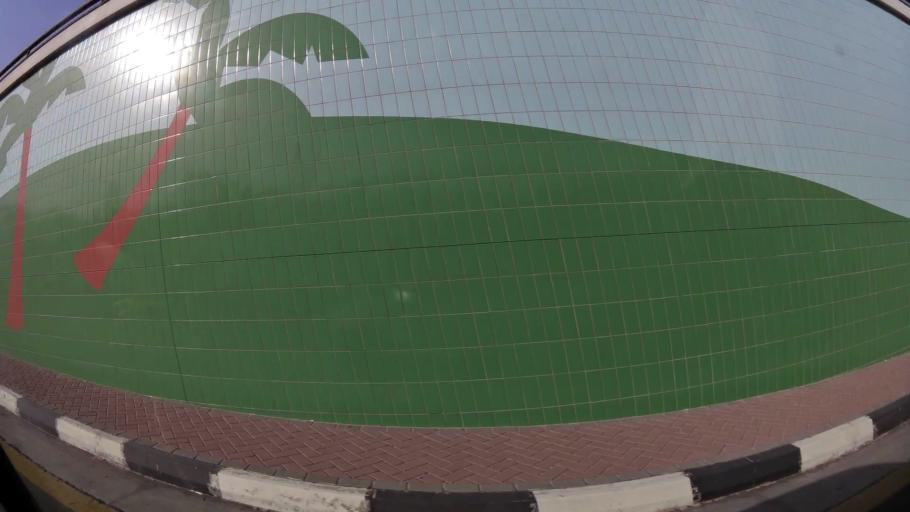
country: AE
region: Ash Shariqah
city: Sharjah
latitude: 25.2505
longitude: 55.3471
